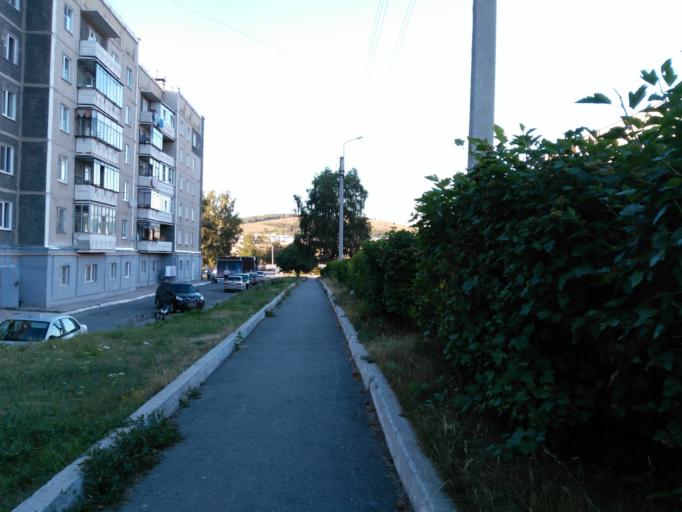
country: RU
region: Bashkortostan
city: Uchaly
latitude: 54.3189
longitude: 59.3701
